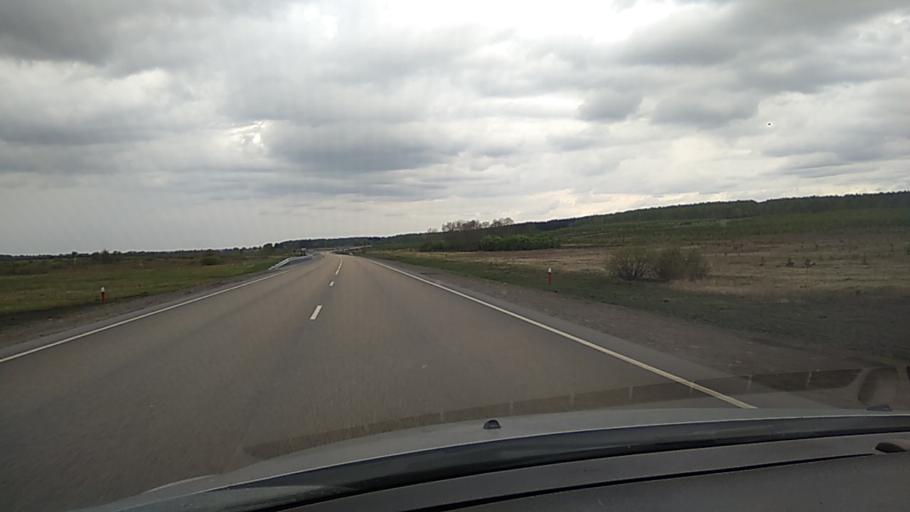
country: RU
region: Kurgan
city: Kataysk
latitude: 56.2974
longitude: 62.4207
